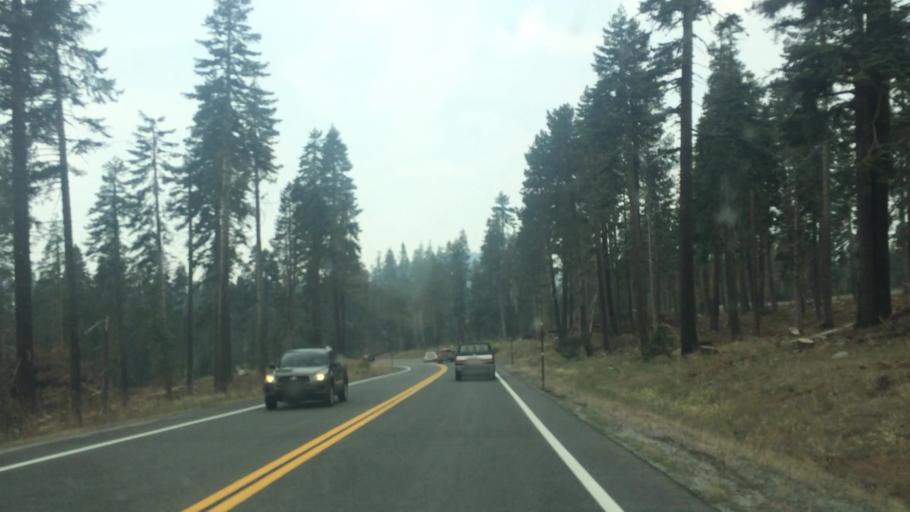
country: US
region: California
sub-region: El Dorado County
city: South Lake Tahoe
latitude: 38.6283
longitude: -120.2106
